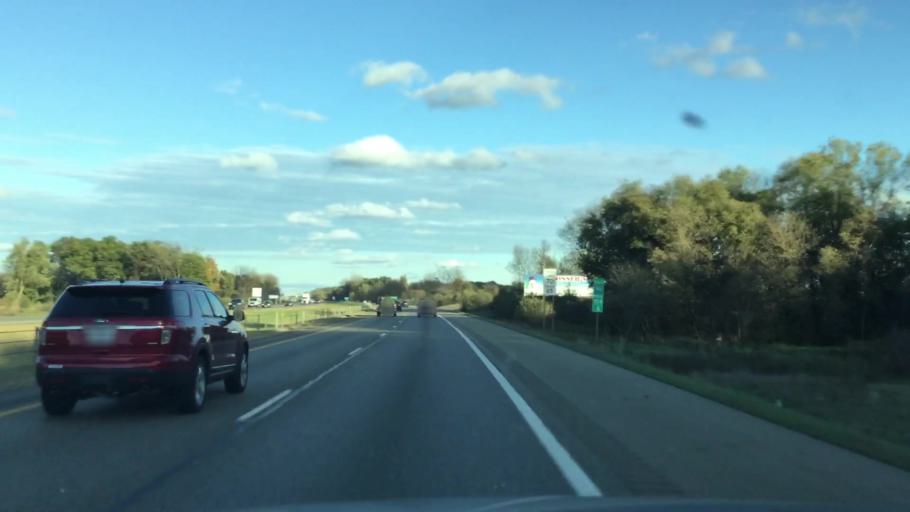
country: US
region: Michigan
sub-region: Calhoun County
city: Brownlee Park
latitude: 42.2981
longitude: -85.0677
